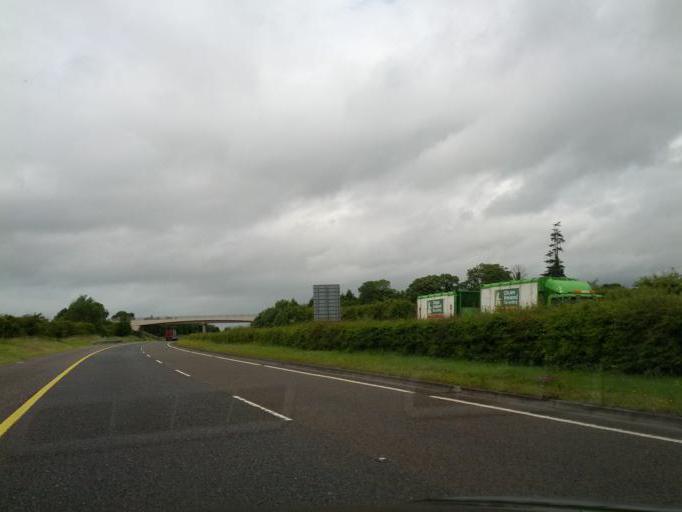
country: IE
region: Munster
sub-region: An Clar
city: Newmarket on Fergus
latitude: 52.7573
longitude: -8.9135
